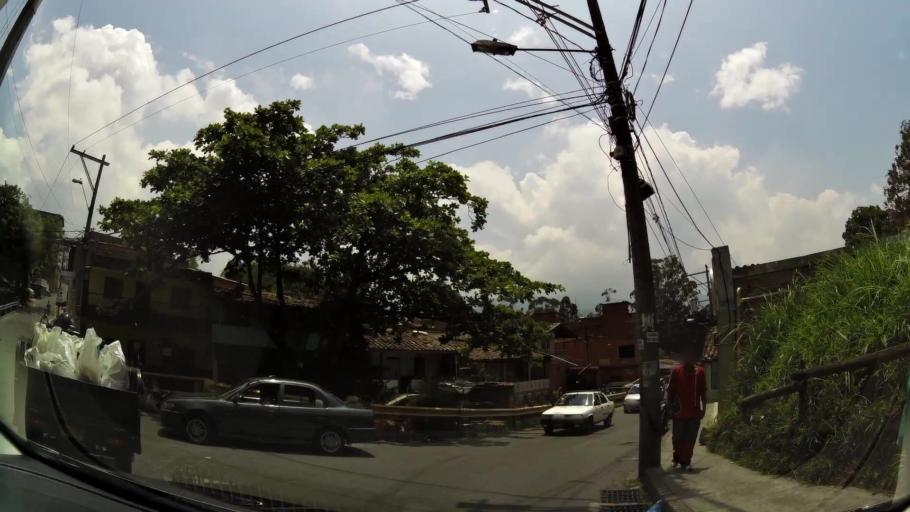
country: CO
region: Antioquia
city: Itagui
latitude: 6.1768
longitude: -75.6117
